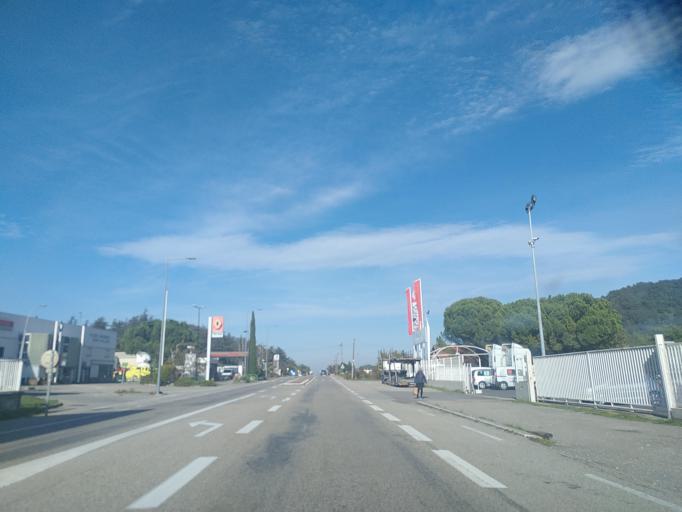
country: FR
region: Rhone-Alpes
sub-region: Departement de l'Ardeche
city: Sarras
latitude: 45.1938
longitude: 4.8144
